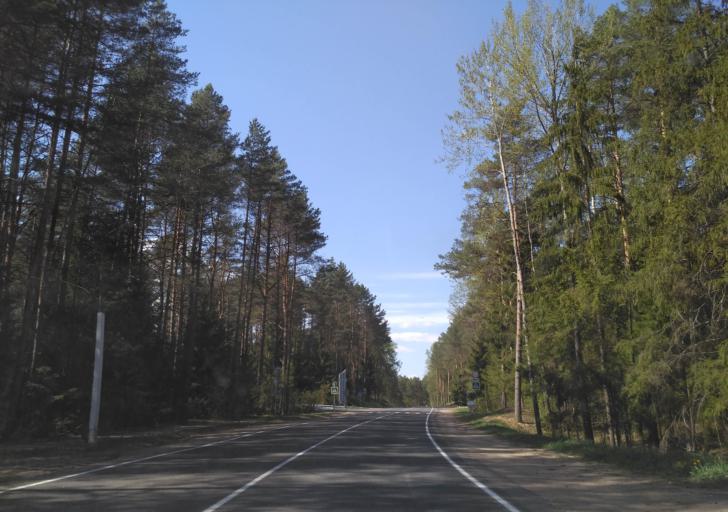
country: BY
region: Minsk
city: Narach
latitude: 54.9115
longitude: 26.7248
